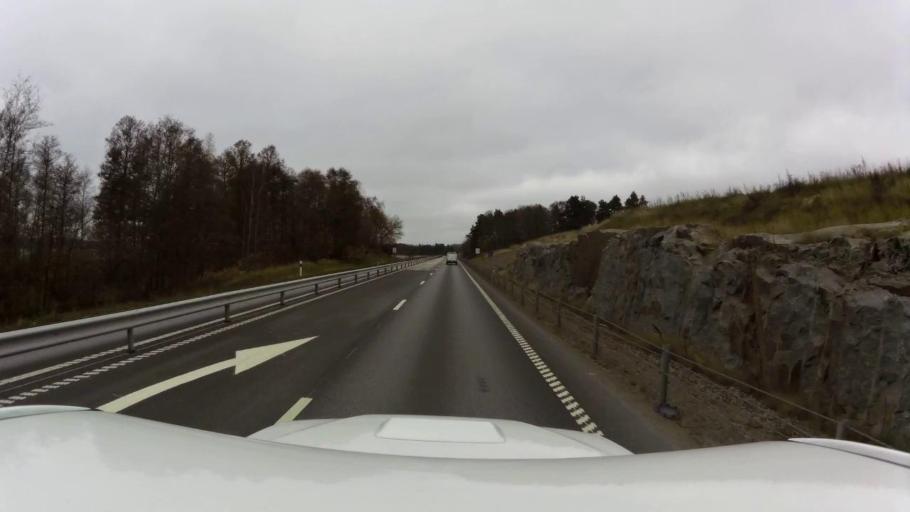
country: SE
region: OEstergoetland
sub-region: Kinda Kommun
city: Rimforsa
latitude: 58.1491
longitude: 15.6805
